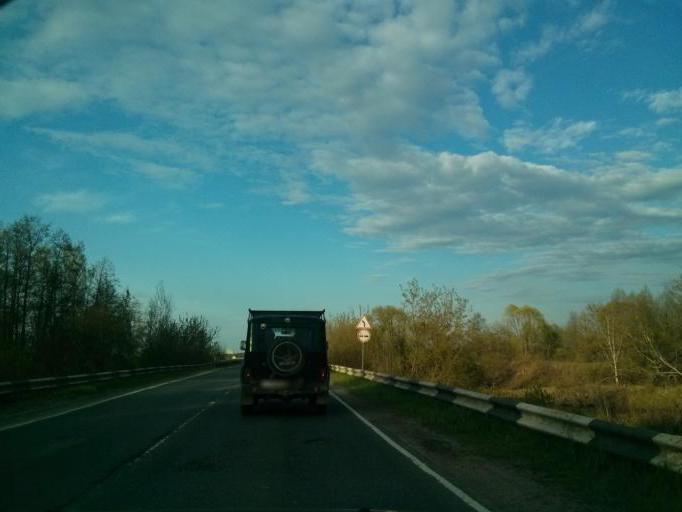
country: RU
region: Nizjnij Novgorod
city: Navashino
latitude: 55.6182
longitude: 42.2277
